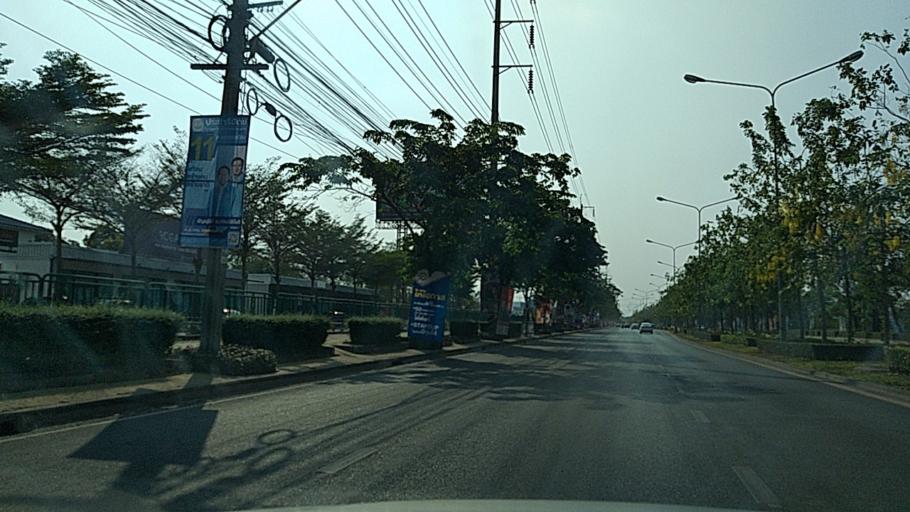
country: TH
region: Bangkok
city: Don Mueang
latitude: 13.9310
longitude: 100.5736
